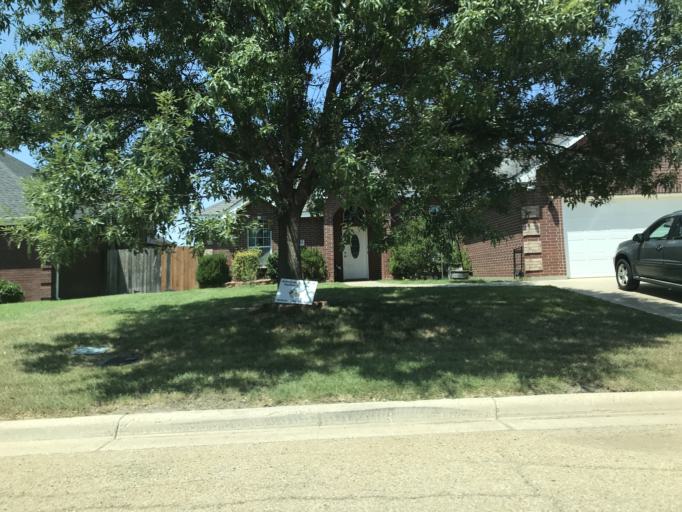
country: US
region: Texas
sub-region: Taylor County
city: Abilene
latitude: 32.4902
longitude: -99.6865
